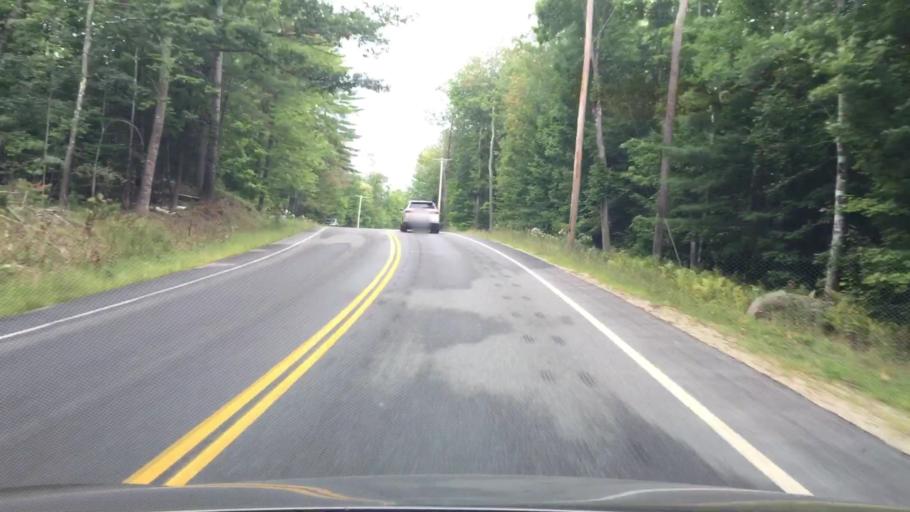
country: US
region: Maine
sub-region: Oxford County
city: Hartford
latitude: 44.3551
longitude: -70.3046
